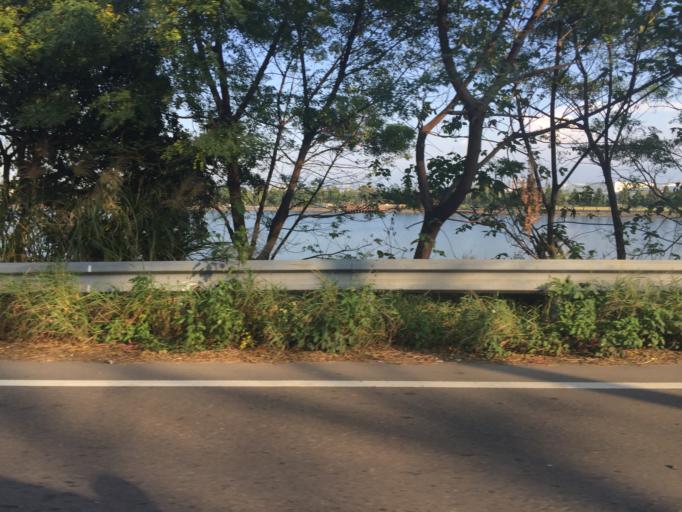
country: TW
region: Taiwan
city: Daxi
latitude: 24.9137
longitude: 121.2544
